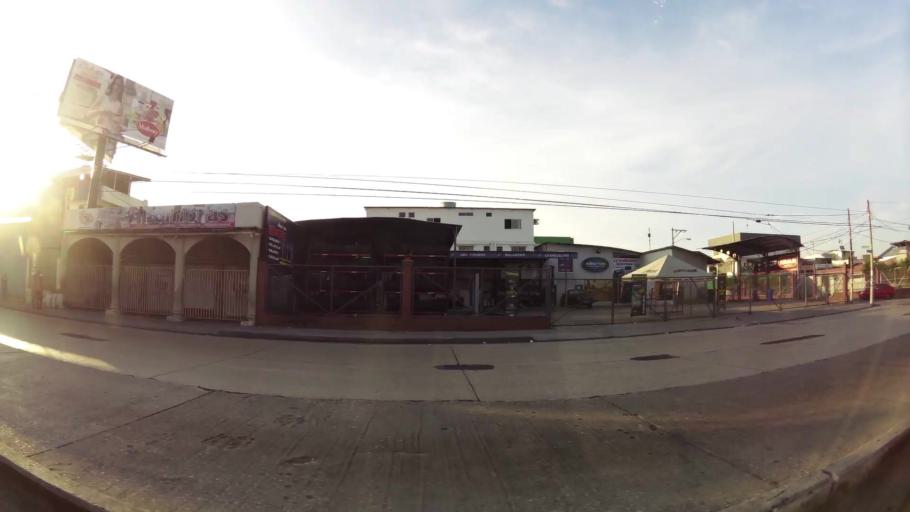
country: EC
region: Guayas
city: Eloy Alfaro
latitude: -2.1518
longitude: -79.8938
